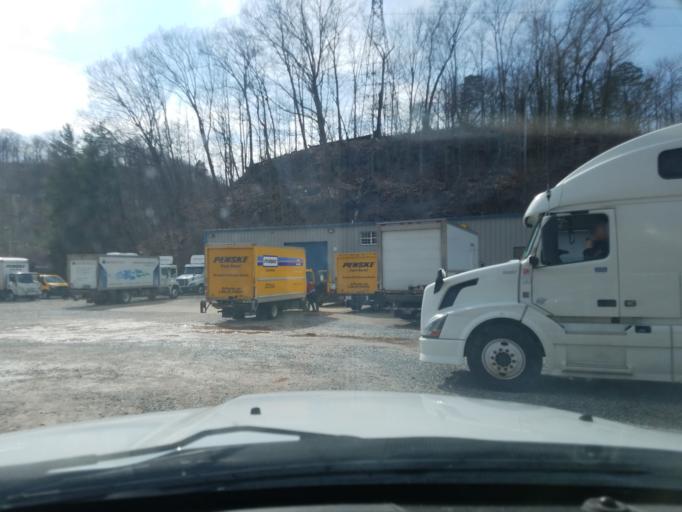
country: US
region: West Virginia
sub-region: Kanawha County
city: Cross Lanes
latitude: 38.4076
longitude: -81.7932
